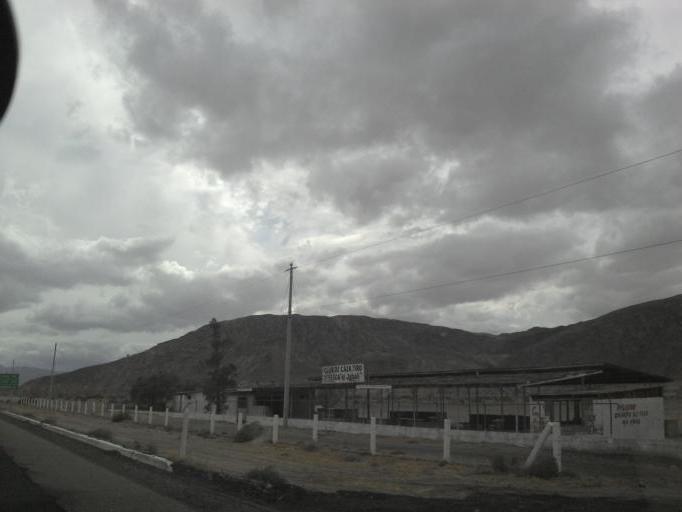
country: MX
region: Baja California
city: Progreso
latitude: 32.5865
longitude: -115.7070
